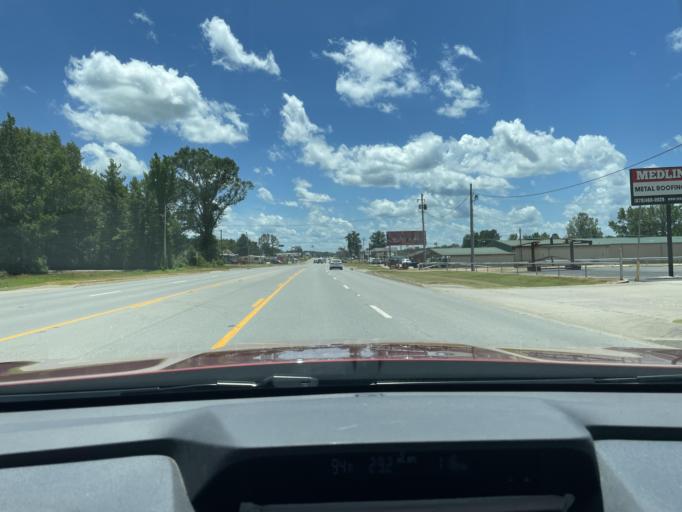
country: US
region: Arkansas
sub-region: Drew County
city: Monticello
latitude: 33.6430
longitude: -91.8010
